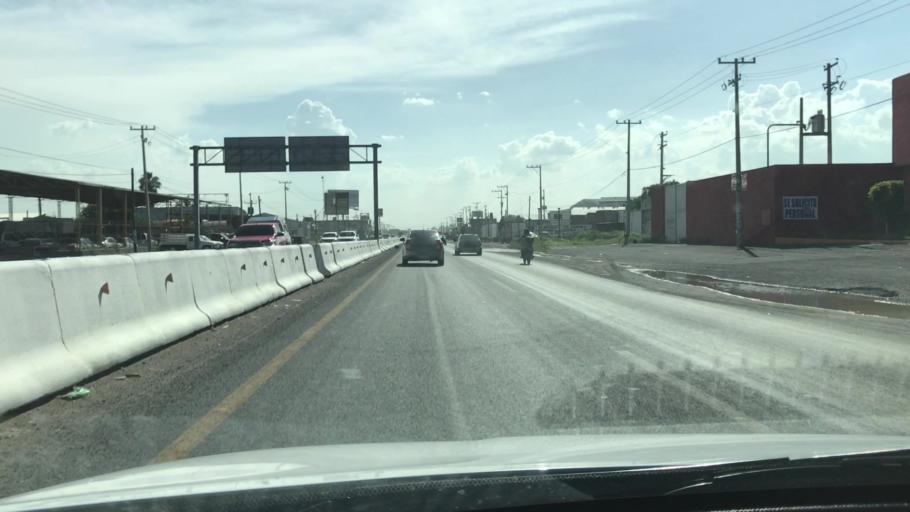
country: MX
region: Guanajuato
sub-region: Celaya
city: Colonia Pedro Maria Anaya
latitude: 20.5181
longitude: -100.8569
